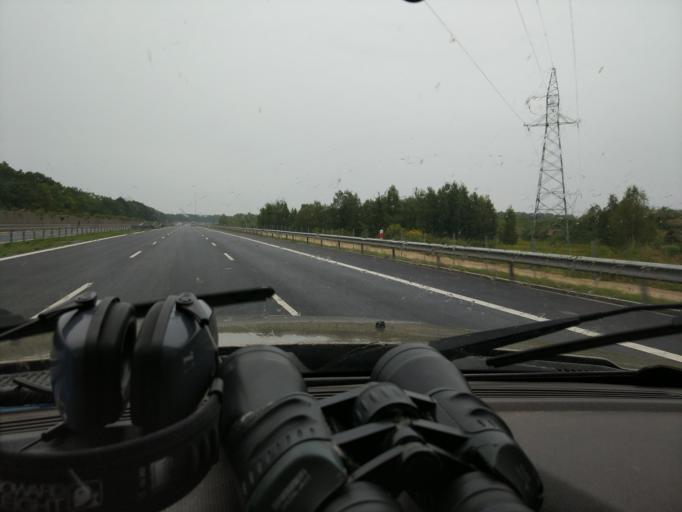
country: PL
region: Masovian Voivodeship
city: Zielonka
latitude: 52.3344
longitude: 21.1571
